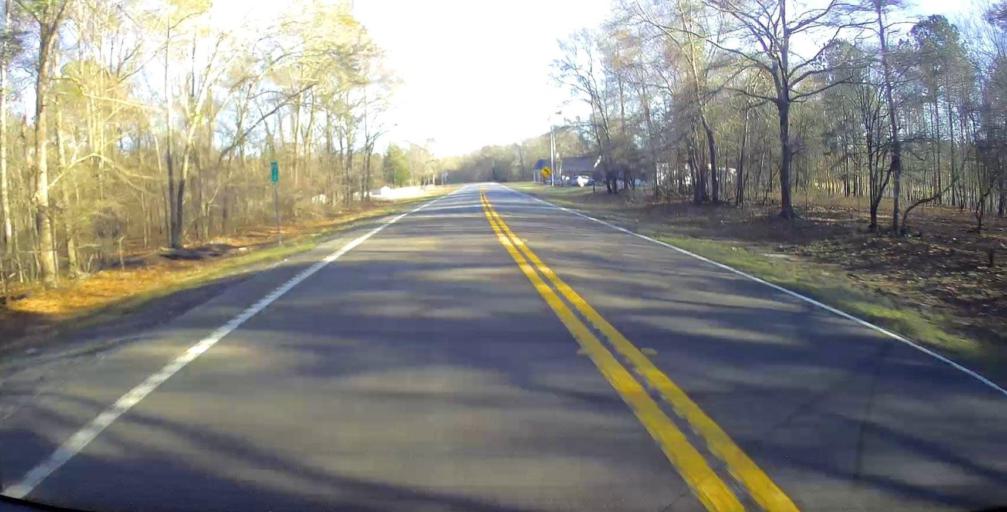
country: US
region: Georgia
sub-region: Taylor County
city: Butler
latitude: 32.4792
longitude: -84.3899
